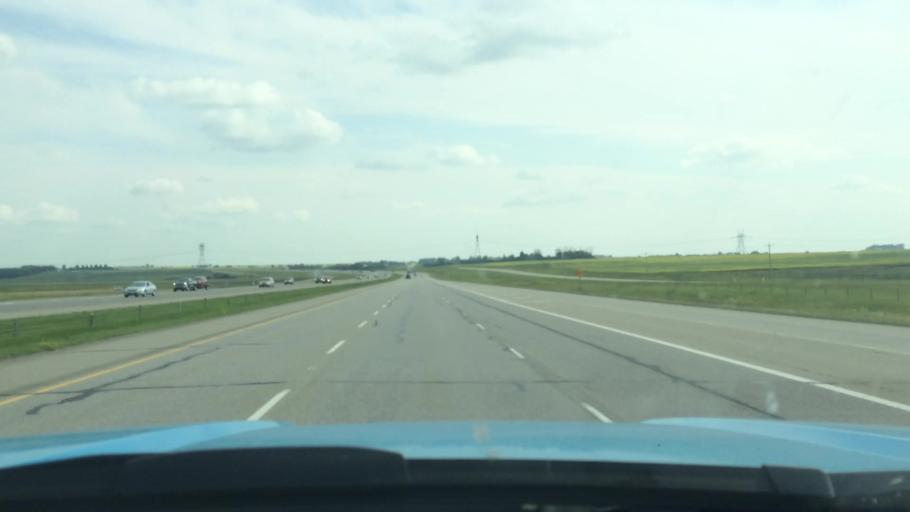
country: CA
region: Alberta
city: Crossfield
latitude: 51.4680
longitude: -114.0264
